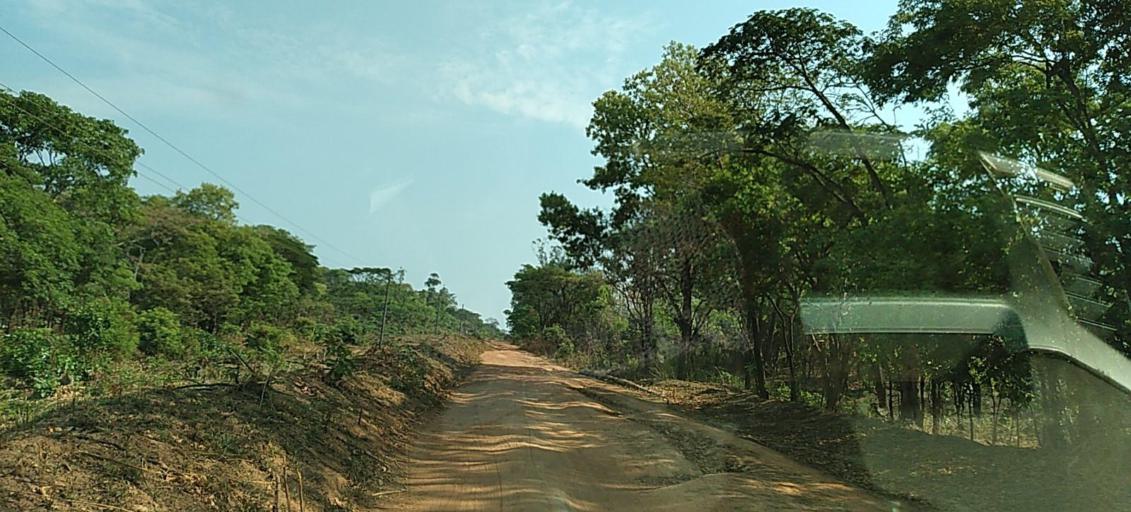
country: ZM
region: Copperbelt
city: Kalulushi
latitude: -13.0065
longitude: 27.8131
